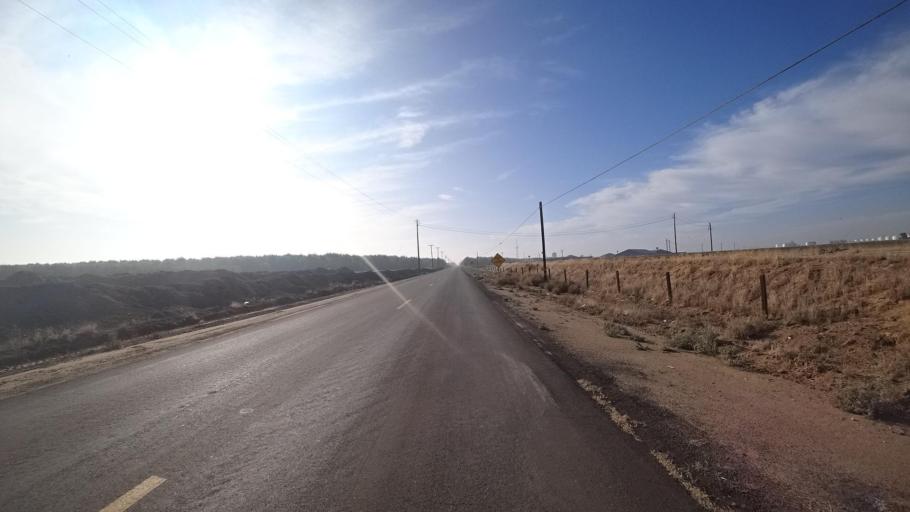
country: US
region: California
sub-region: Kern County
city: McFarland
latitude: 35.6399
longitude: -119.2045
